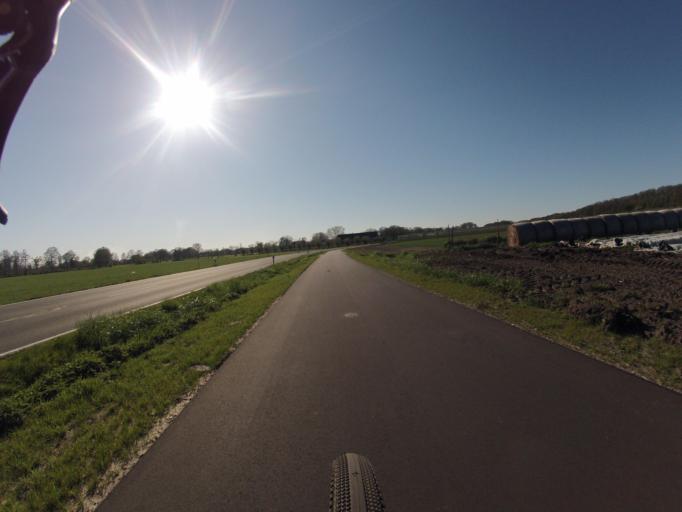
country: DE
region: North Rhine-Westphalia
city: Ibbenburen
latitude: 52.2247
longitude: 7.7249
